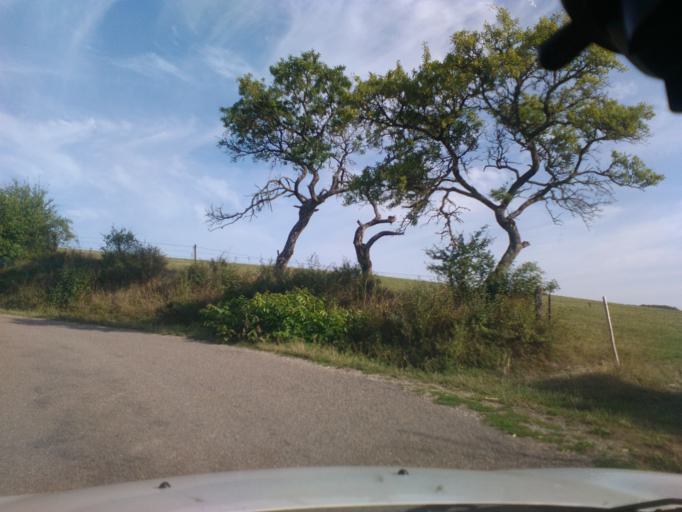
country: FR
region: Lorraine
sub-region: Departement des Vosges
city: Mirecourt
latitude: 48.2807
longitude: 6.0396
